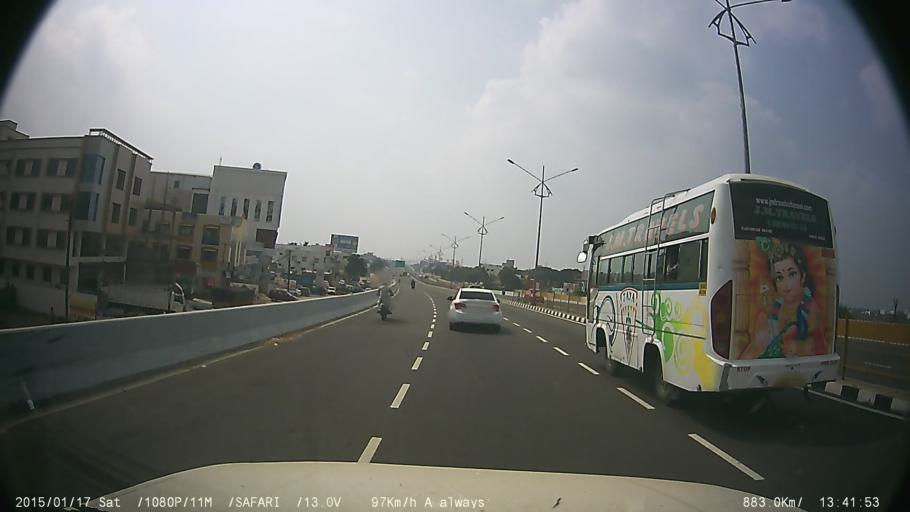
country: IN
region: Tamil Nadu
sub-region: Vellore
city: Vellore
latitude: 12.9347
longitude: 79.1476
